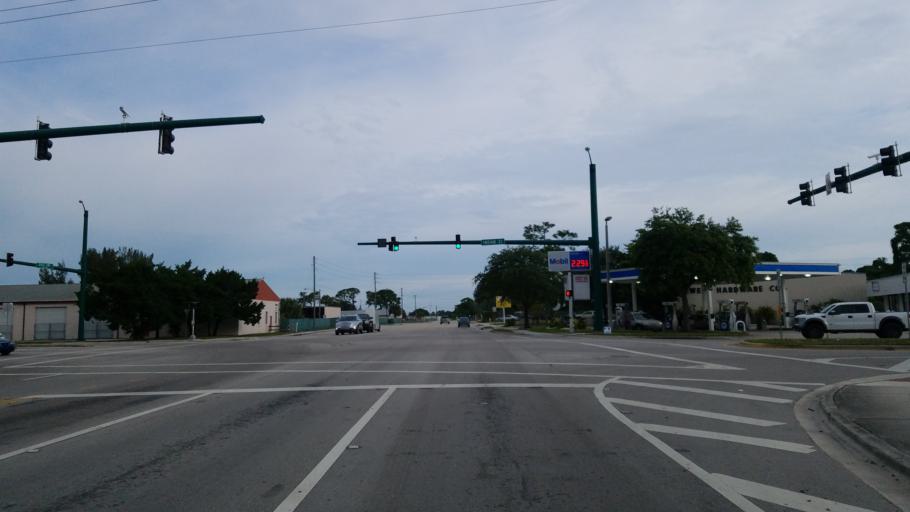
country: US
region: Florida
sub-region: Martin County
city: Port Salerno
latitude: 27.1678
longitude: -80.2217
